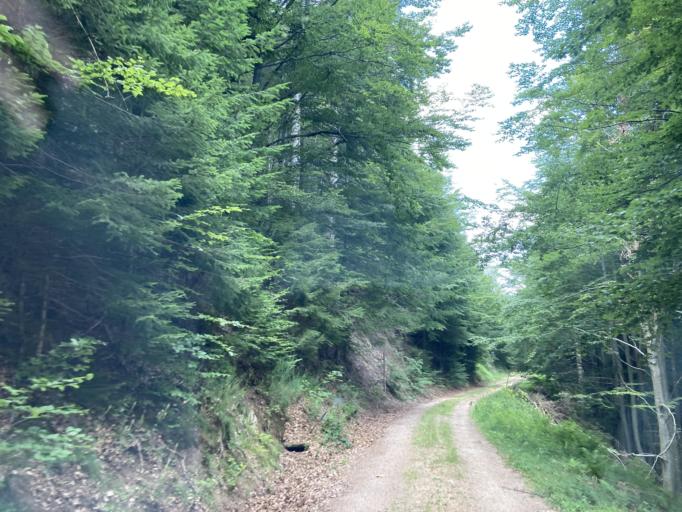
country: DE
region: Baden-Wuerttemberg
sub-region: Freiburg Region
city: Schonach im Schwarzwald
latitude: 48.1583
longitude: 8.1550
